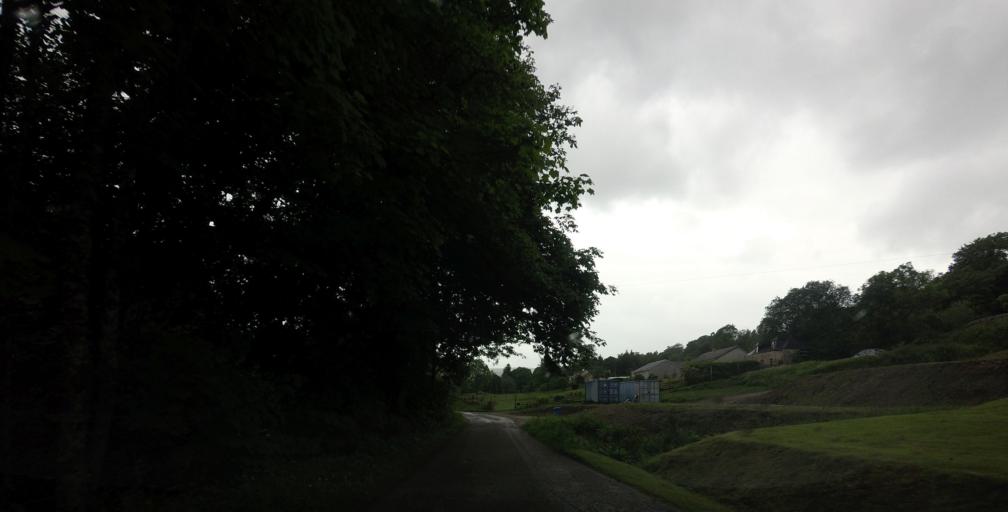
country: GB
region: Scotland
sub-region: Argyll and Bute
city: Oban
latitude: 56.7003
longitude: -5.5708
